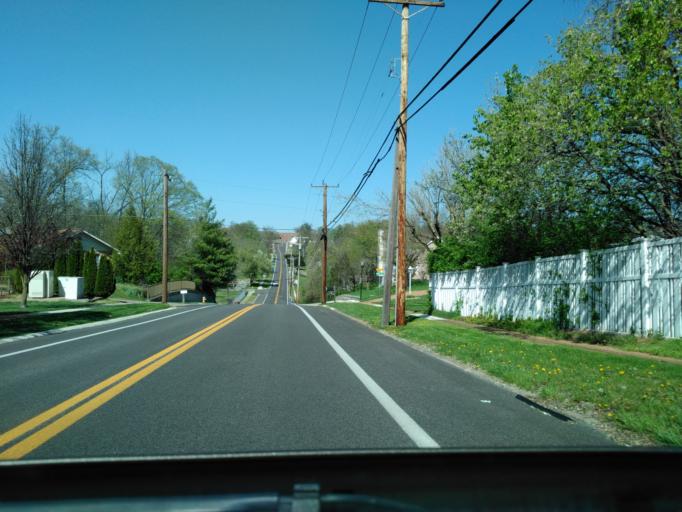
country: US
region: Missouri
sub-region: Saint Louis County
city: Concord
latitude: 38.4958
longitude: -90.3648
